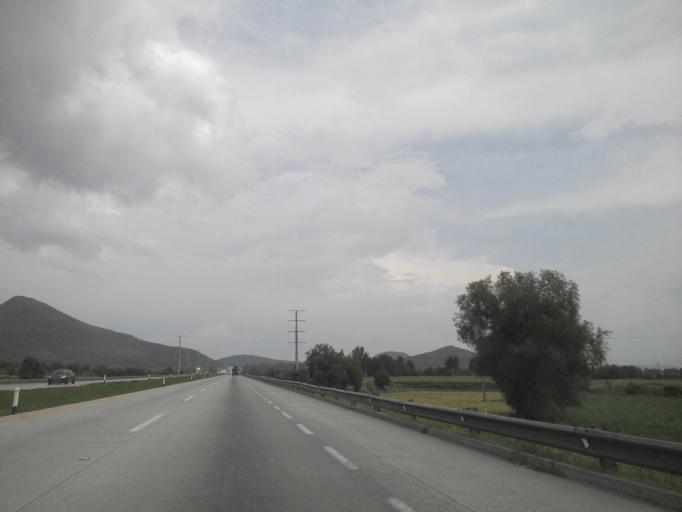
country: MX
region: Hidalgo
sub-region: Atitalaquia
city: Tezoquipa
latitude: 20.0466
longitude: -99.1858
